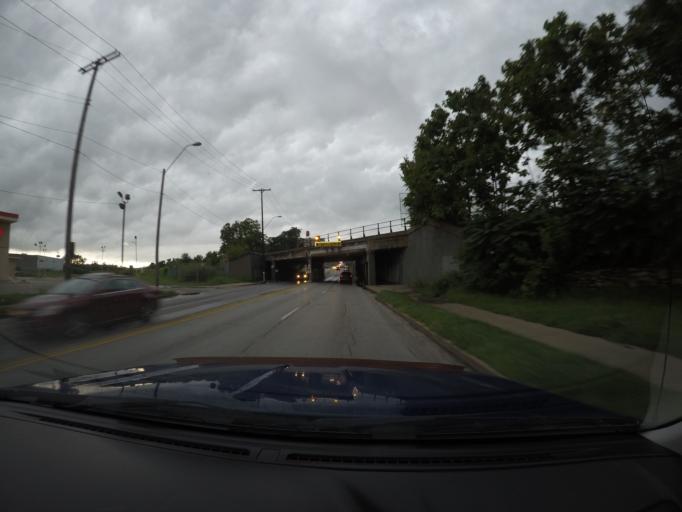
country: US
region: Missouri
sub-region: Clay County
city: North Kansas City
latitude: 39.1049
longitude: -94.5124
